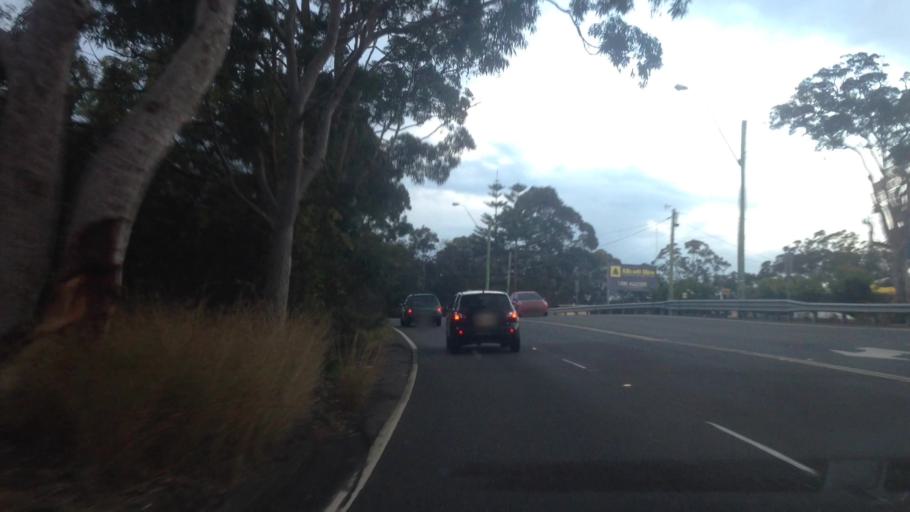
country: AU
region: New South Wales
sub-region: Wyong Shire
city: Kanwal
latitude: -33.2514
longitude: 151.4905
